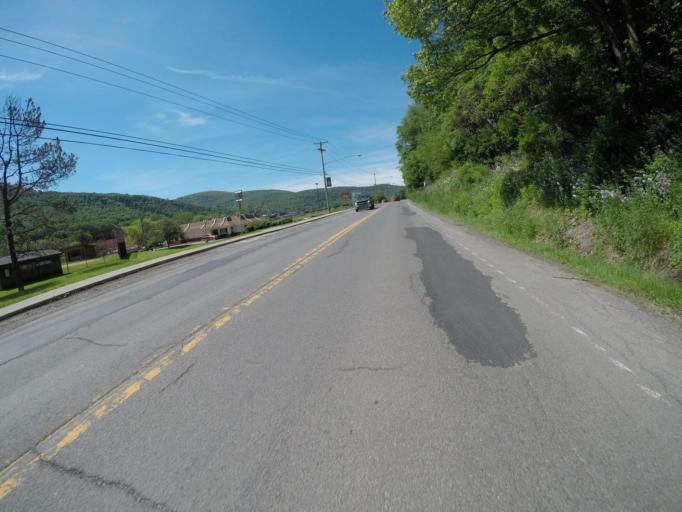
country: US
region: New York
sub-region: Delaware County
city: Delhi
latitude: 42.2683
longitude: -74.9223
